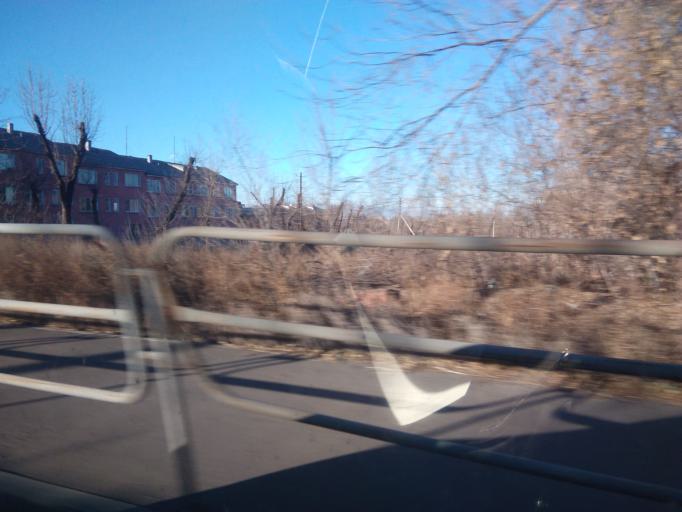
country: RU
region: Chelyabinsk
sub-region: Gorod Magnitogorsk
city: Magnitogorsk
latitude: 53.3885
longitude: 59.0584
